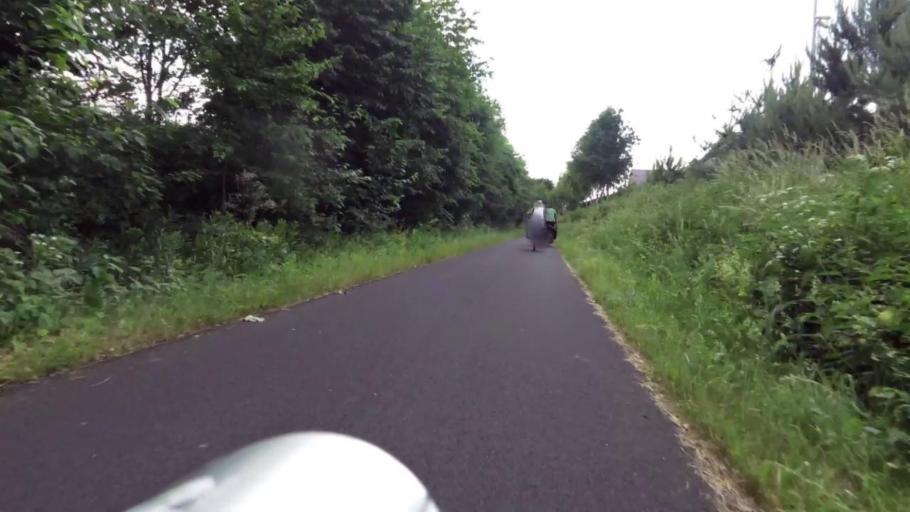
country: PL
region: Kujawsko-Pomorskie
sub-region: Powiat torunski
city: Lubianka
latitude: 53.1111
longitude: 18.5101
